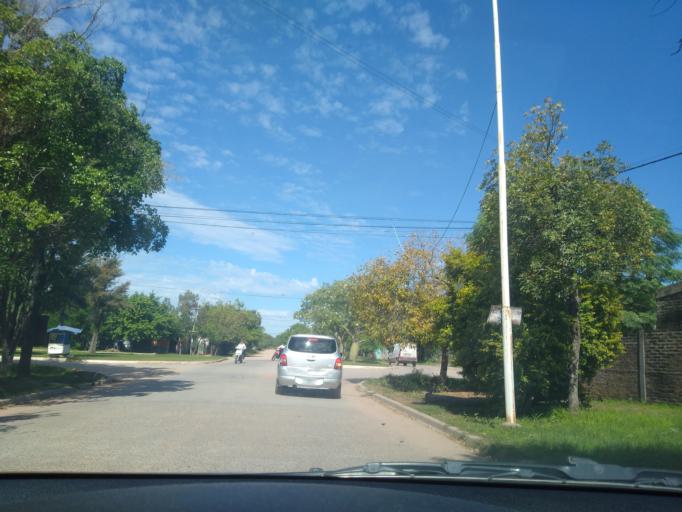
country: AR
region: Chaco
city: Presidencia Roque Saenz Pena
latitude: -26.7800
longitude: -60.4263
